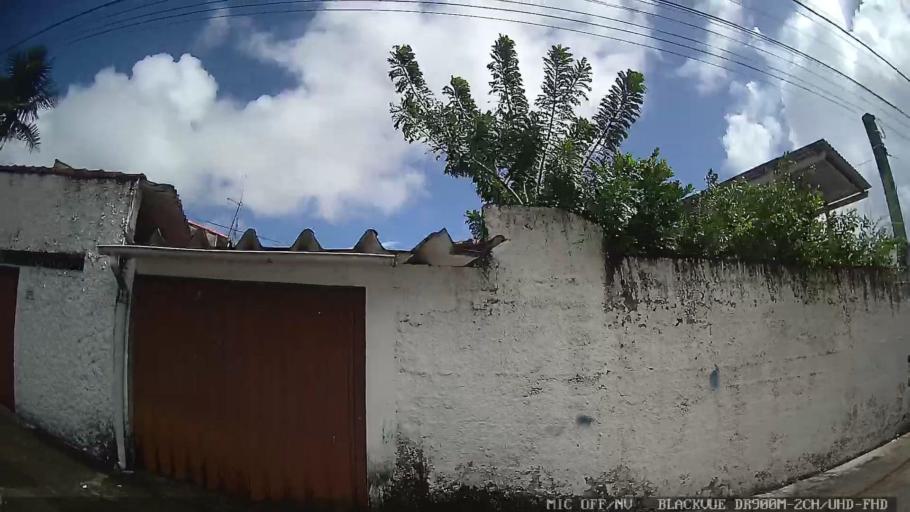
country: BR
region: Sao Paulo
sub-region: Itanhaem
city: Itanhaem
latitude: -24.1900
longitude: -46.8088
